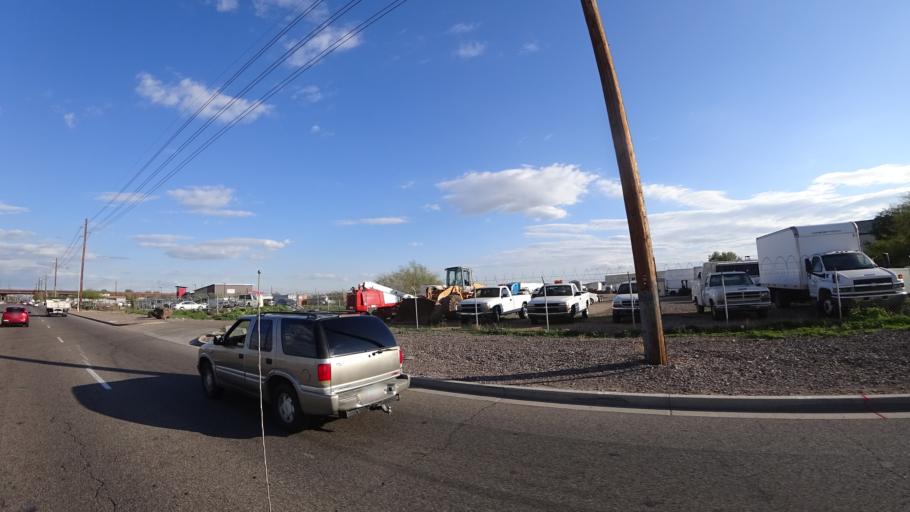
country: US
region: Arizona
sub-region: Maricopa County
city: Glendale
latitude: 33.5526
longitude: -112.2083
